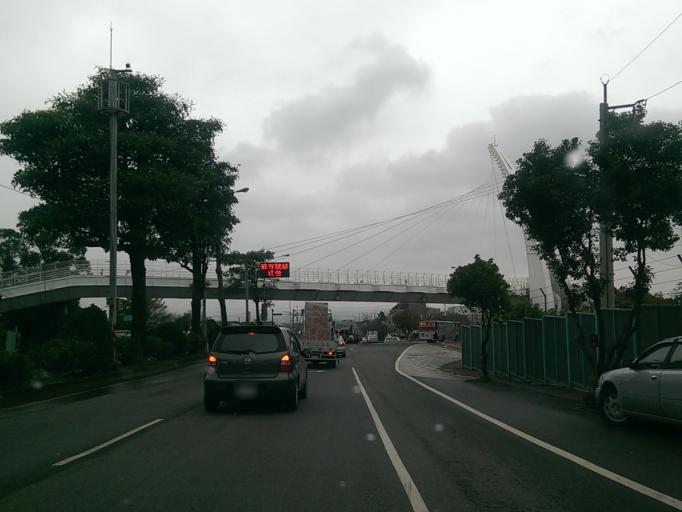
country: TW
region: Taiwan
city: Fengyuan
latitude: 24.2502
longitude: 120.5990
